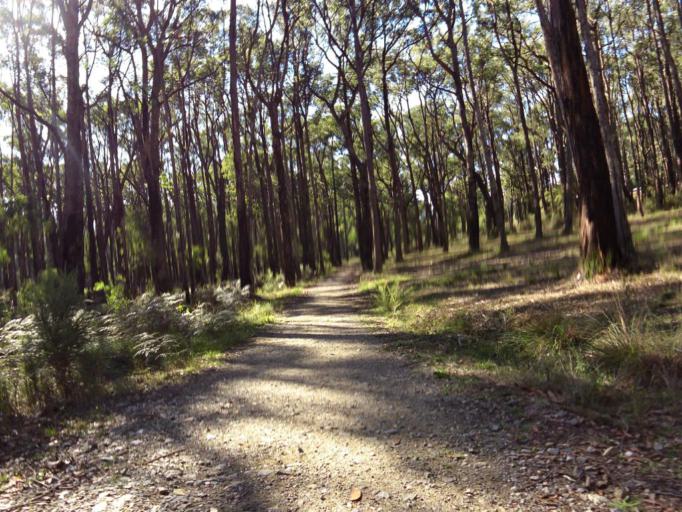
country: AU
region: Victoria
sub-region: Cardinia
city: Cockatoo
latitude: -37.9318
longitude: 145.4811
